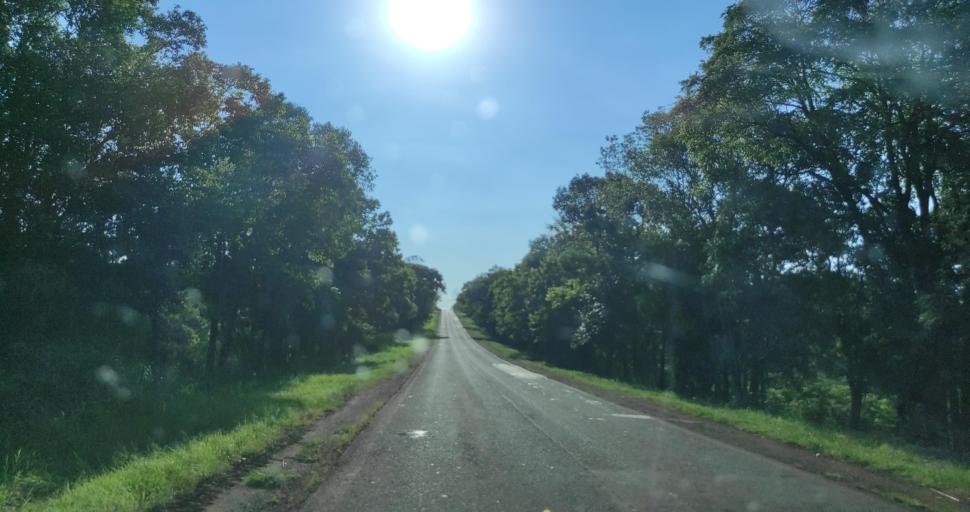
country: AR
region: Misiones
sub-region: Departamento de Eldorado
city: Eldorado
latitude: -26.4001
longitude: -54.4043
